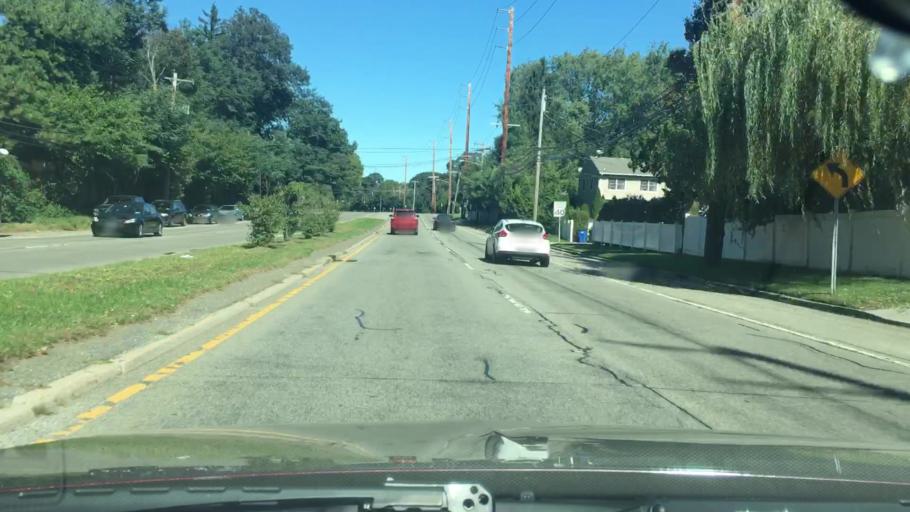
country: US
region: New York
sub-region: Nassau County
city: Roslyn Estates
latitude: 40.8018
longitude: -73.6689
